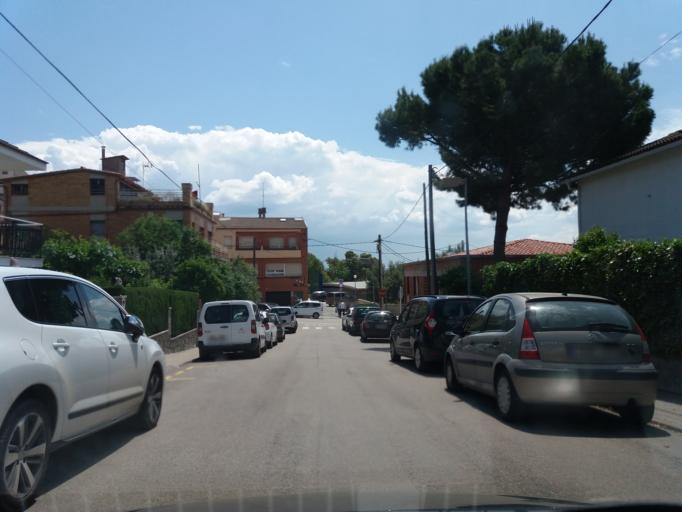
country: ES
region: Catalonia
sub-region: Provincia de Barcelona
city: Sant Joan de Vilatorrada
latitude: 41.7429
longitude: 1.8014
